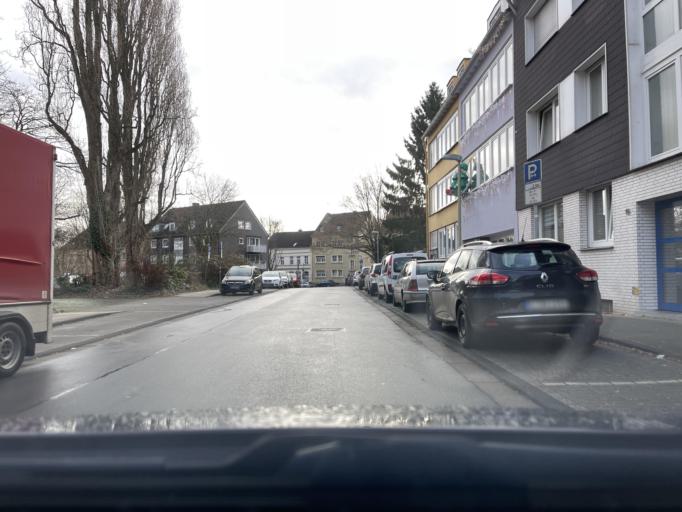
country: DE
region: North Rhine-Westphalia
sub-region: Regierungsbezirk Munster
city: Bottrop
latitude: 51.4752
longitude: 6.9540
